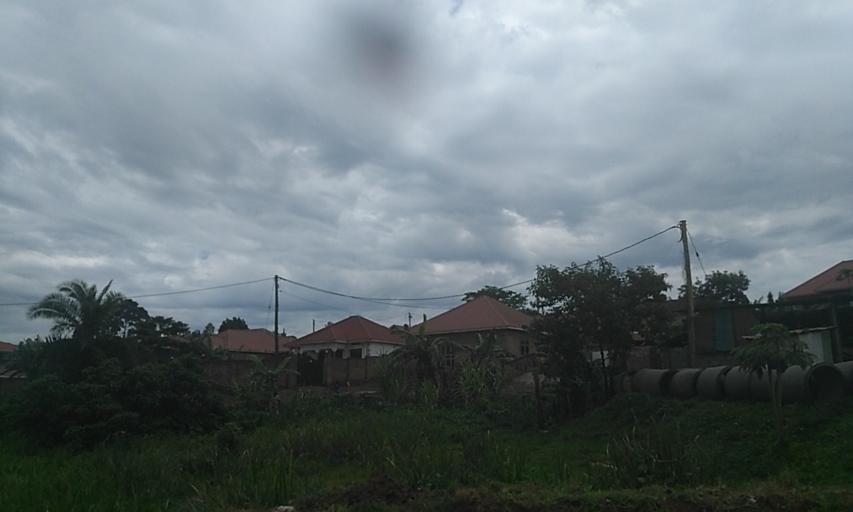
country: UG
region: Central Region
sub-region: Wakiso District
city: Bweyogerere
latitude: 0.3976
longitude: 32.6738
